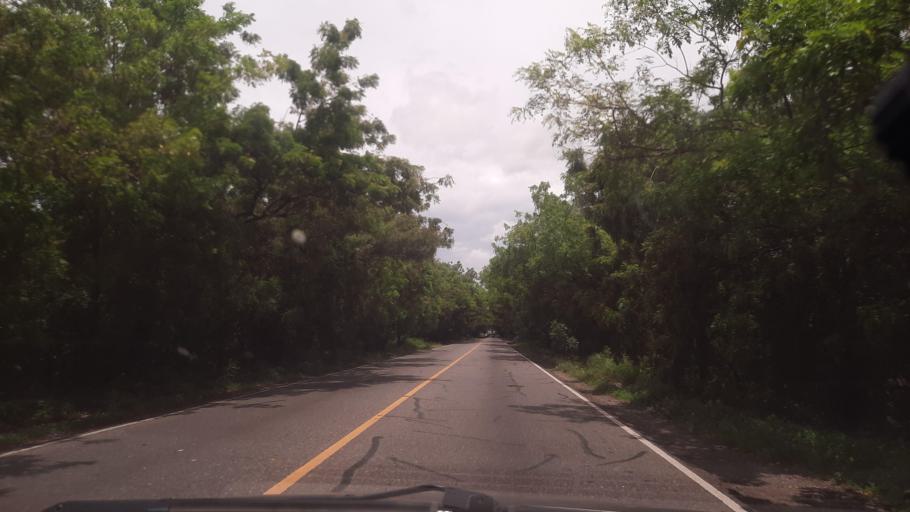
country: GT
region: Zacapa
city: Estanzuela
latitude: 15.0216
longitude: -89.5810
